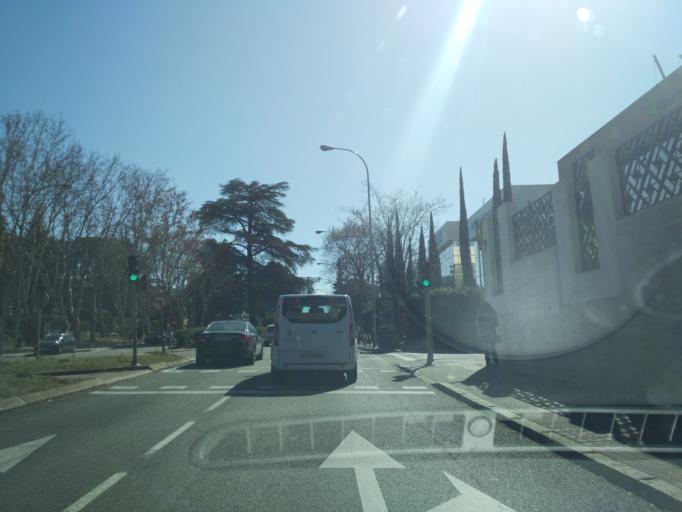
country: ES
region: Madrid
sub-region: Provincia de Madrid
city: Ciudad Lineal
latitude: 40.4512
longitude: -3.6527
